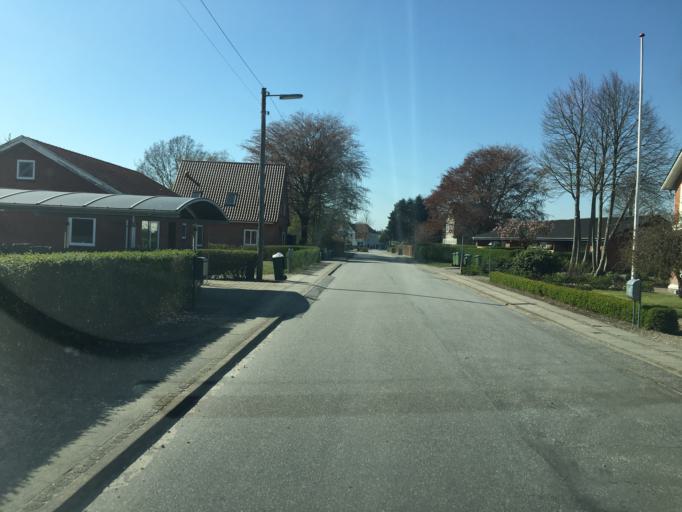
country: DK
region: South Denmark
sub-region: Aabenraa Kommune
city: Rodekro
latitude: 55.0233
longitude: 9.3136
